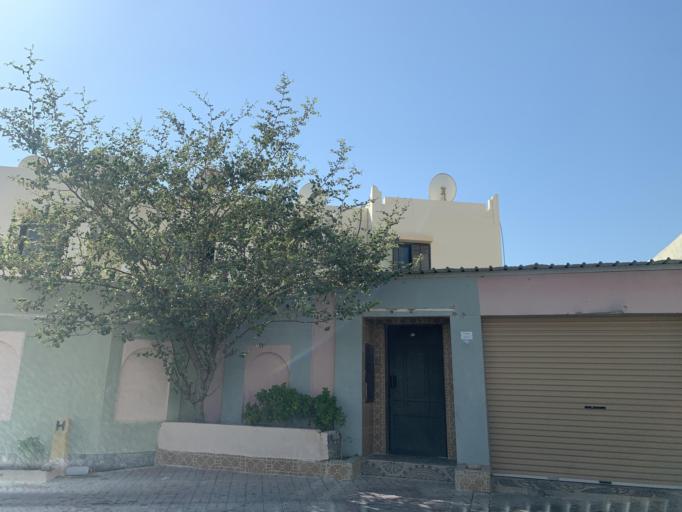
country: BH
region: Central Governorate
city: Madinat Hamad
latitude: 26.1269
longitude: 50.4804
